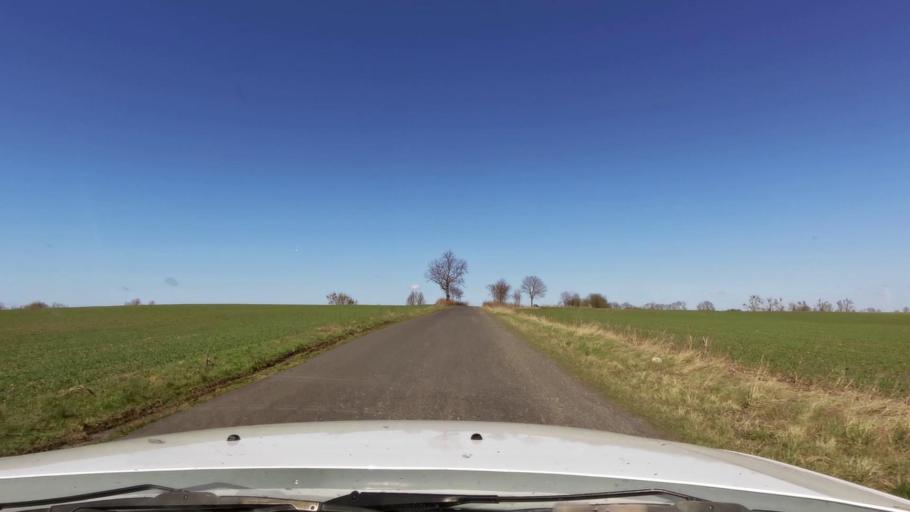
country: PL
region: West Pomeranian Voivodeship
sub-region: Powiat gryfinski
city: Cedynia
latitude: 52.8716
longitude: 14.2876
